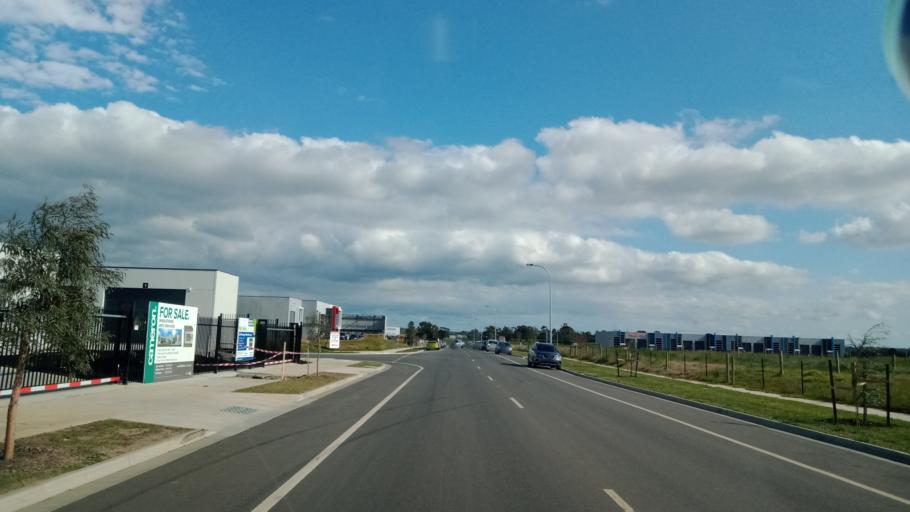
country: AU
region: Victoria
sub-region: Casey
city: Cranbourne West
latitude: -38.0830
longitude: 145.2429
